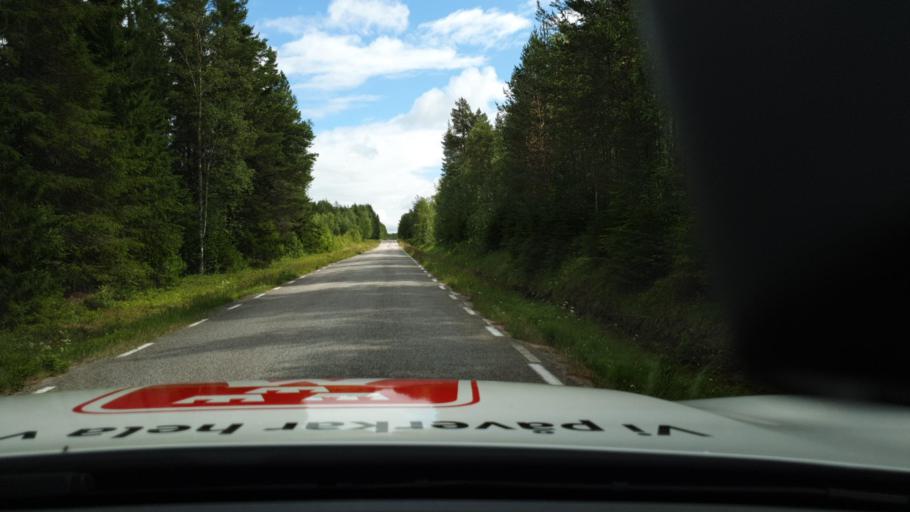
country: SE
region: Norrbotten
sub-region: Lulea Kommun
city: Gammelstad
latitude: 65.4652
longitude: 21.9257
